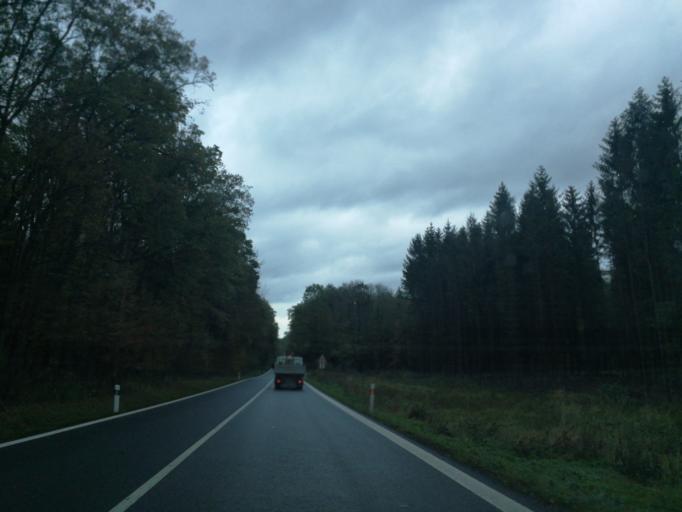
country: CZ
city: Hodslavice
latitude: 49.5192
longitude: 18.0131
